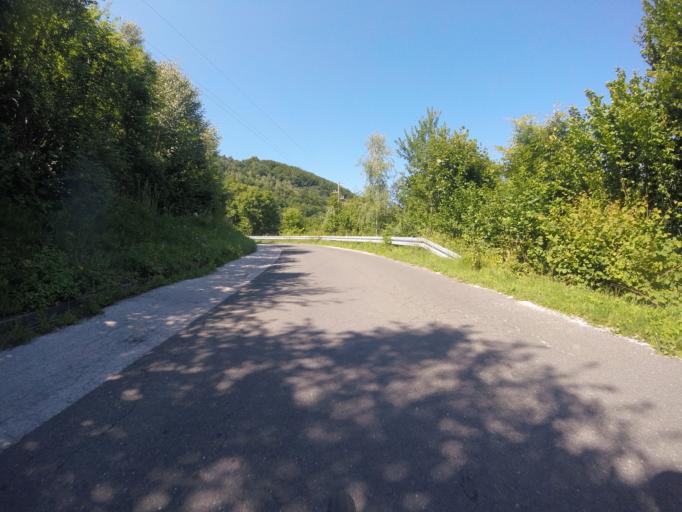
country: SI
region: Brezice
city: Brezice
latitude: 45.8199
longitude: 15.5420
